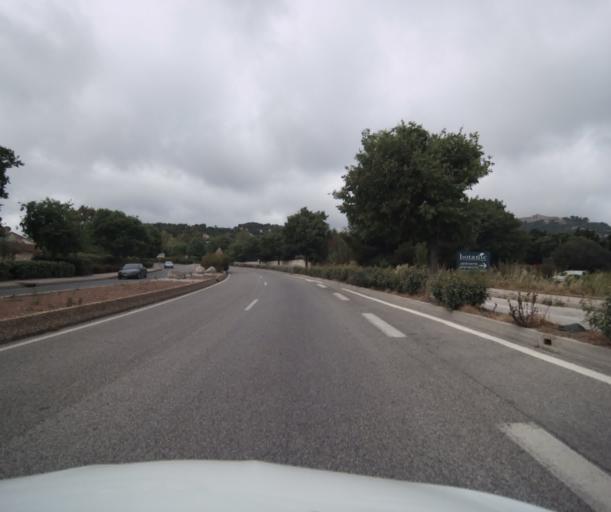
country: FR
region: Provence-Alpes-Cote d'Azur
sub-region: Departement du Var
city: Six-Fours-les-Plages
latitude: 43.1066
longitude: 5.8538
